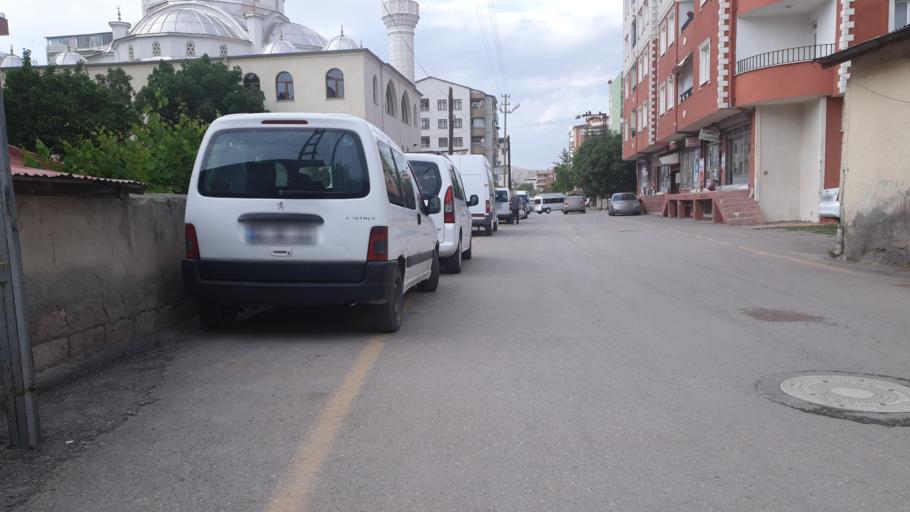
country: TR
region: Van
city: Van
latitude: 38.4909
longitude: 43.3907
